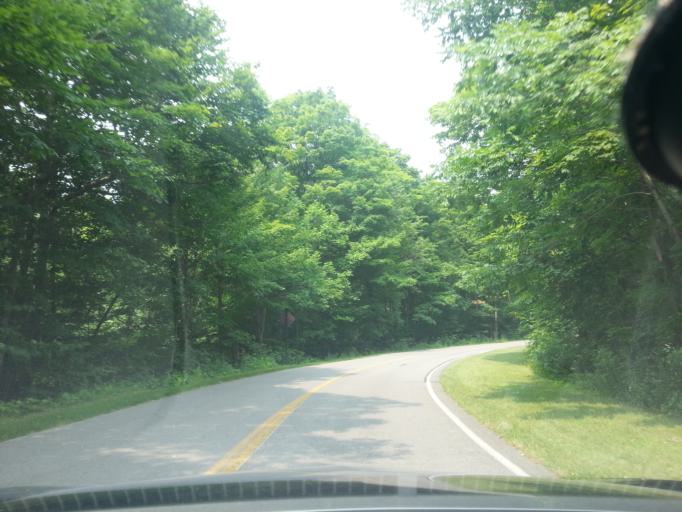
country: CA
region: Quebec
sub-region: Outaouais
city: Wakefield
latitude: 45.5192
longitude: -75.8538
